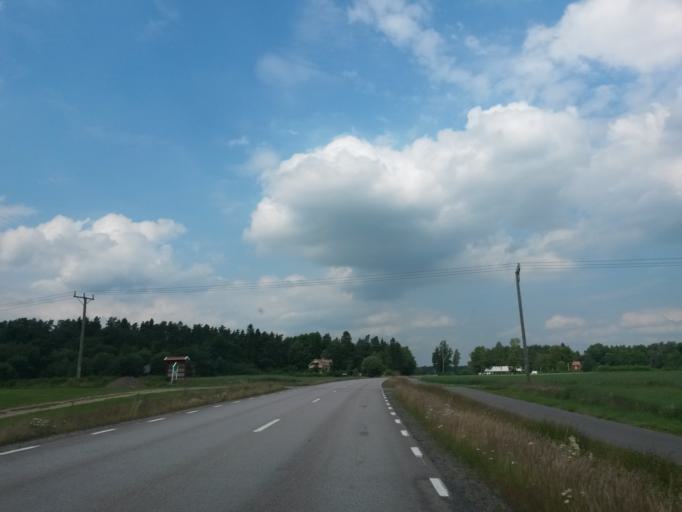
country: SE
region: Vaestra Goetaland
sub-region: Essunga Kommun
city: Nossebro
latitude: 58.1972
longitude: 12.7198
